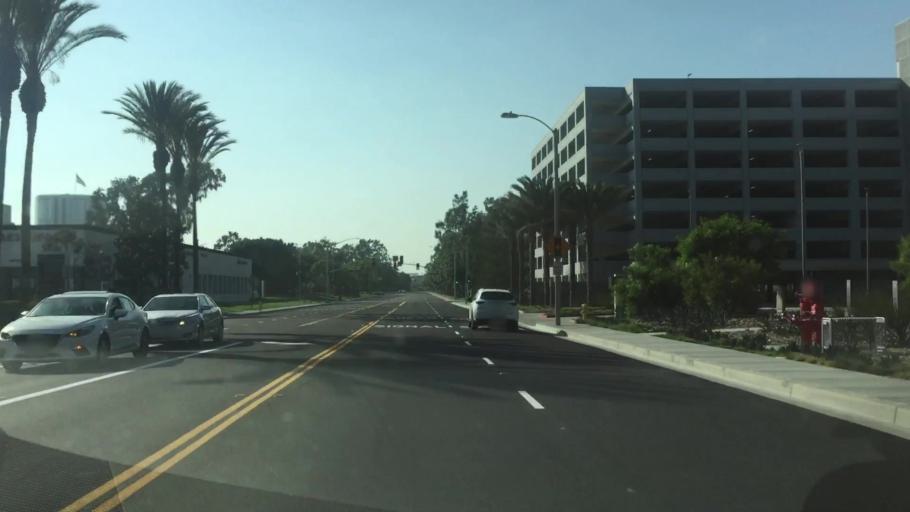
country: US
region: California
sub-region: Orange County
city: Irvine
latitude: 33.6693
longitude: -117.8516
